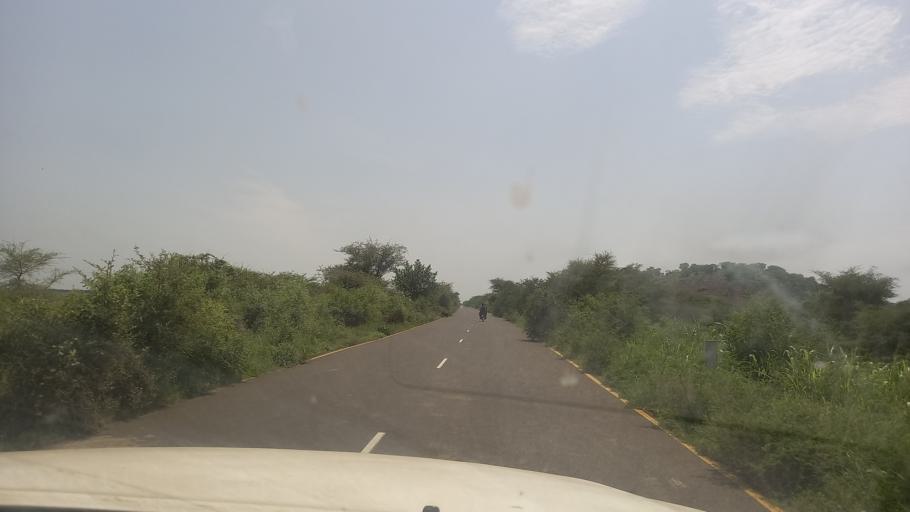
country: ET
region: Gambela
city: Gambela
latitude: 8.2834
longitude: 34.2175
